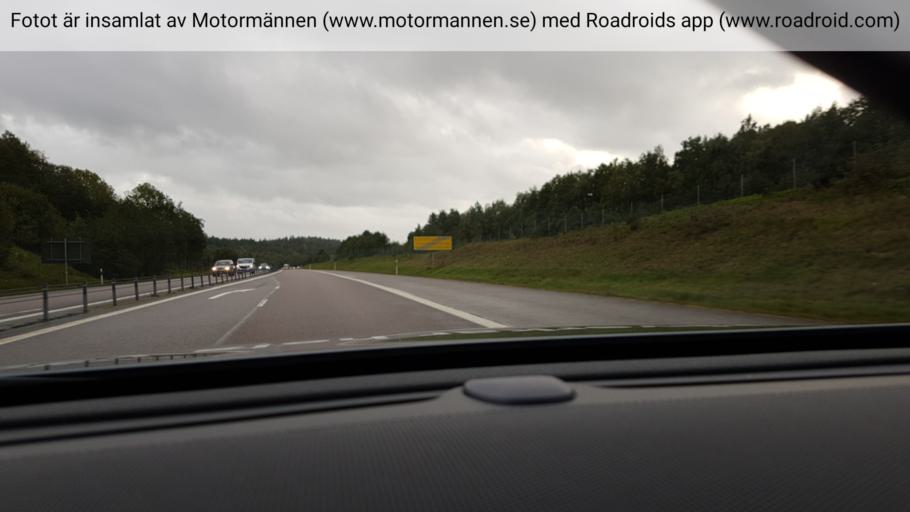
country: SE
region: Vaestra Goetaland
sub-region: Uddevalla Kommun
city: Uddevalla
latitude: 58.3334
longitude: 11.9777
